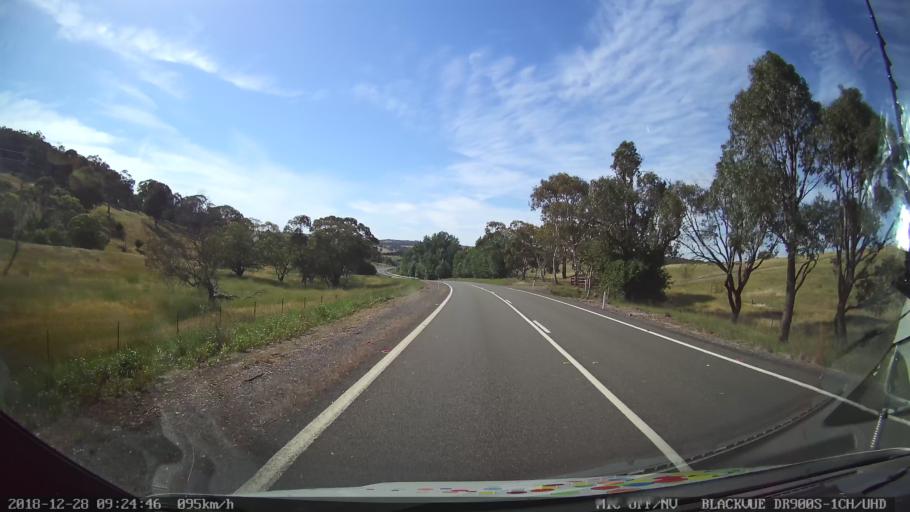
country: AU
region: New South Wales
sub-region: Upper Lachlan Shire
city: Crookwell
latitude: -34.4018
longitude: 149.3831
